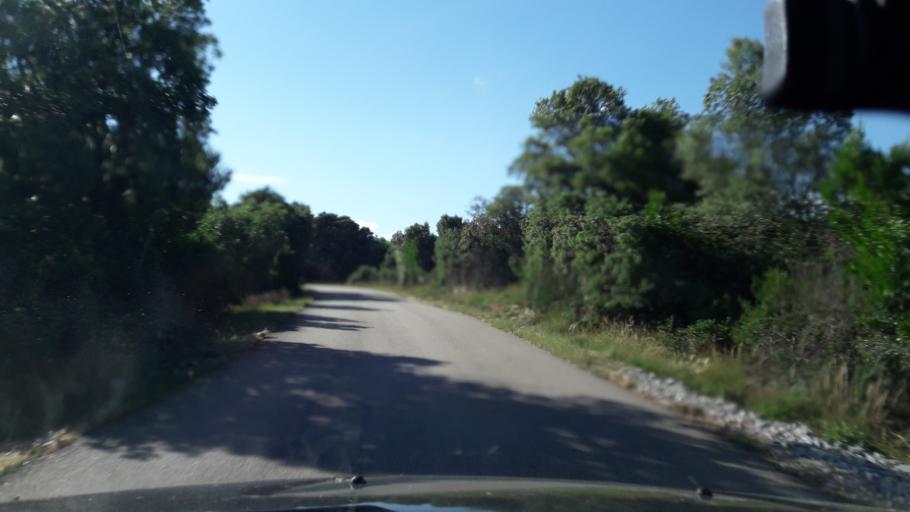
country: FR
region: Languedoc-Roussillon
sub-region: Departement du Gard
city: Saint-Julien-de-Peyrolas
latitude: 44.3693
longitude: 4.5222
